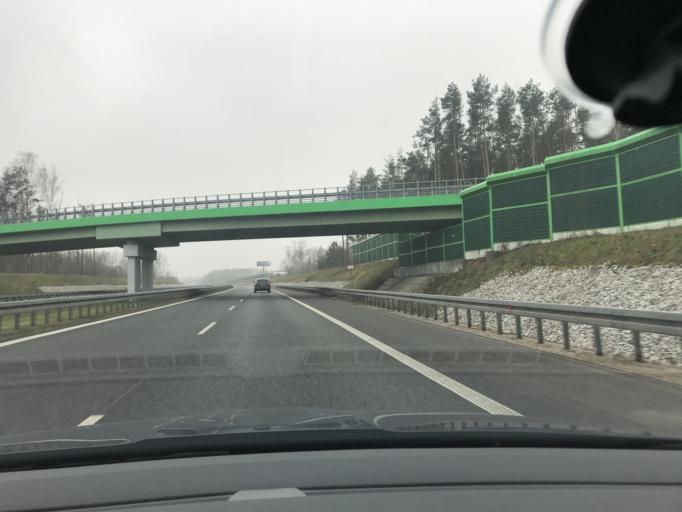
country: PL
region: Lodz Voivodeship
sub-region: Powiat pabianicki
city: Dobron
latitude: 51.6543
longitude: 19.2723
